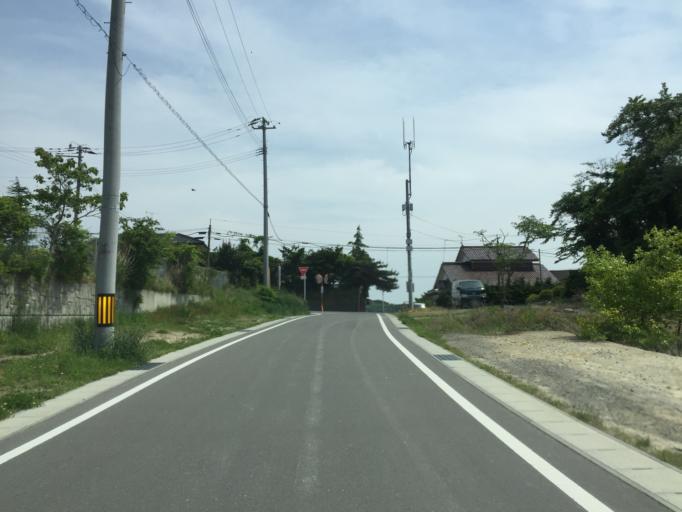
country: JP
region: Miyagi
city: Marumori
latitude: 37.8260
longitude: 140.9568
